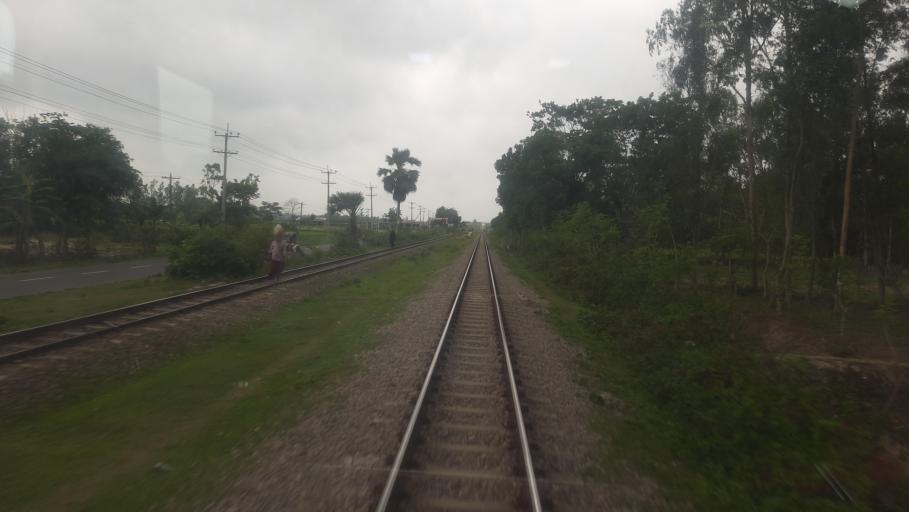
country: BD
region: Dhaka
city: Narsingdi
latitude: 23.9574
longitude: 90.8042
